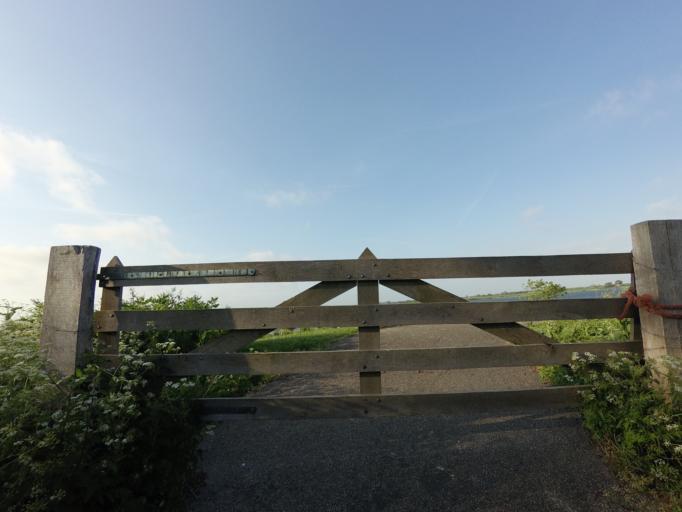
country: NL
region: North Brabant
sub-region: Gemeente Moerdijk
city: Willemstad
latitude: 51.7356
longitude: 4.3545
